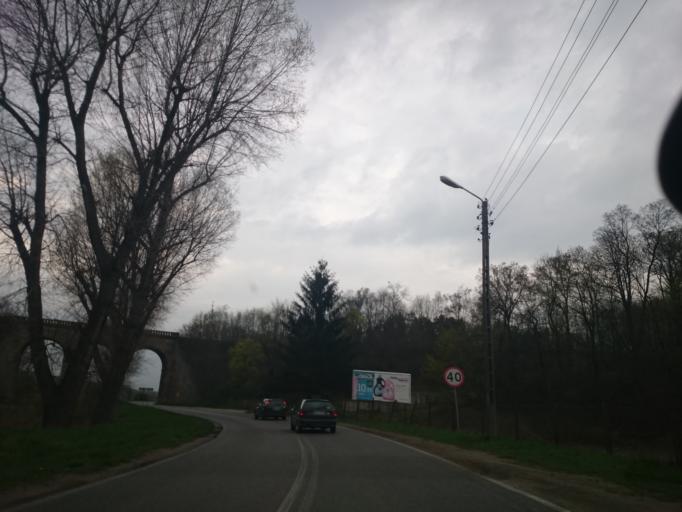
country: PL
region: Lower Silesian Voivodeship
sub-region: Powiat zabkowicki
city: Kamieniec Zabkowicki
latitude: 50.5325
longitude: 16.8649
